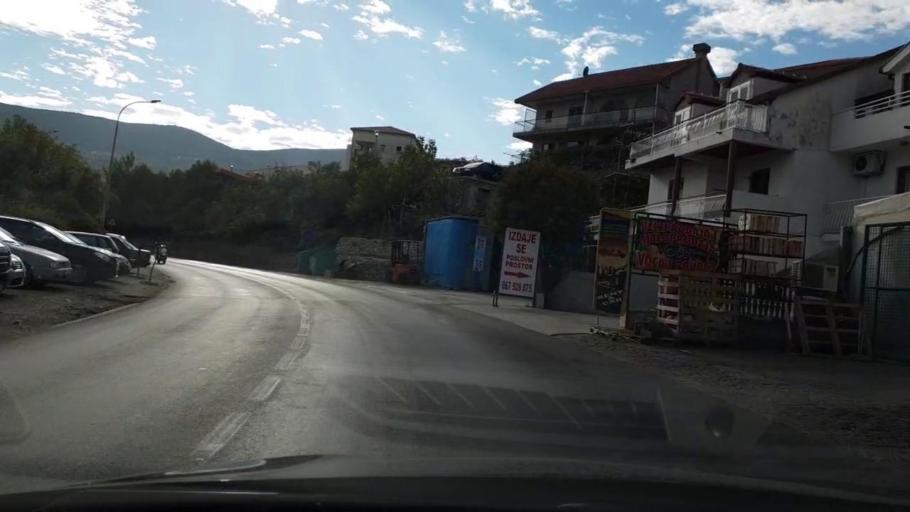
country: ME
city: Igalo
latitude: 42.4616
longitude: 18.5090
